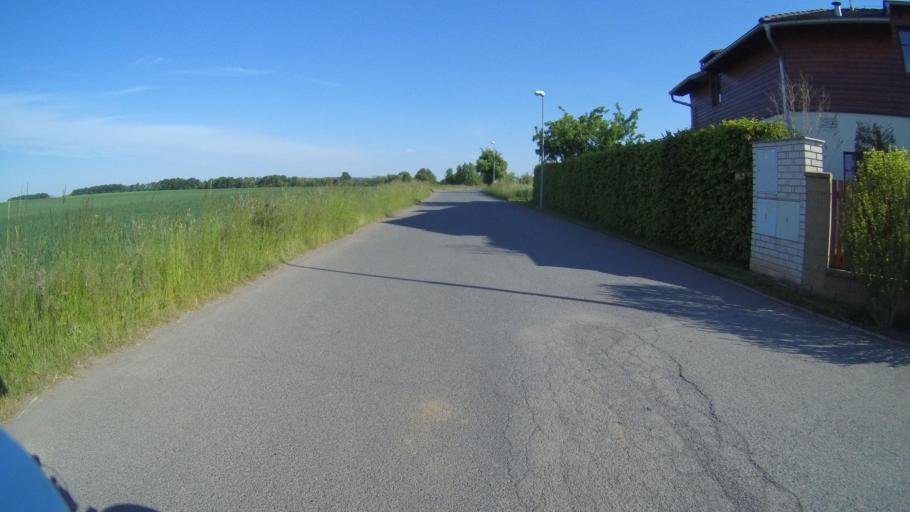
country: CZ
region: Central Bohemia
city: Zdiby
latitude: 50.1609
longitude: 14.4349
